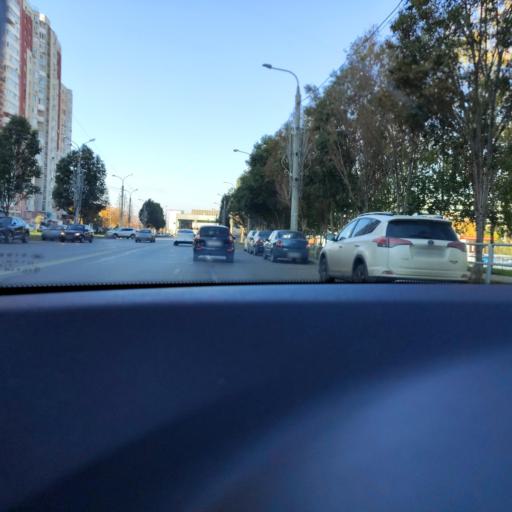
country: RU
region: Samara
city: Samara
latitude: 53.2597
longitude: 50.2111
